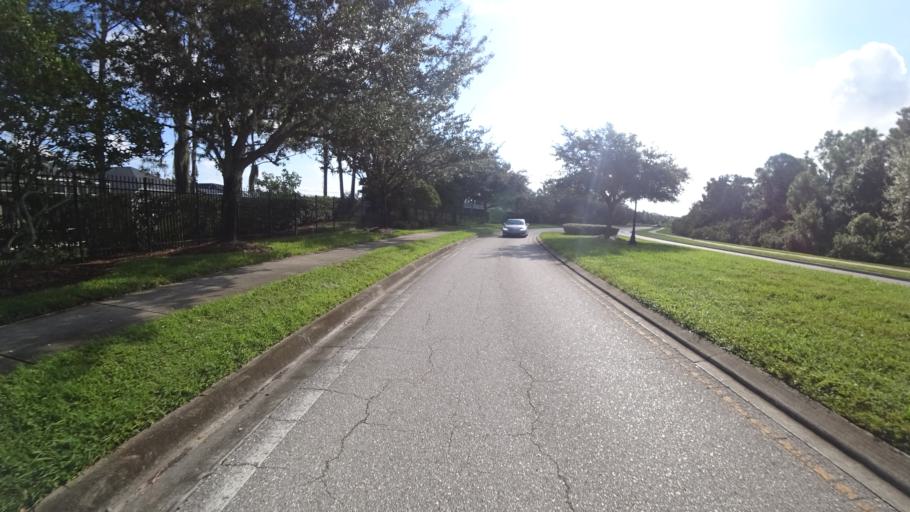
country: US
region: Florida
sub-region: Sarasota County
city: The Meadows
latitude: 27.3990
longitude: -82.4572
